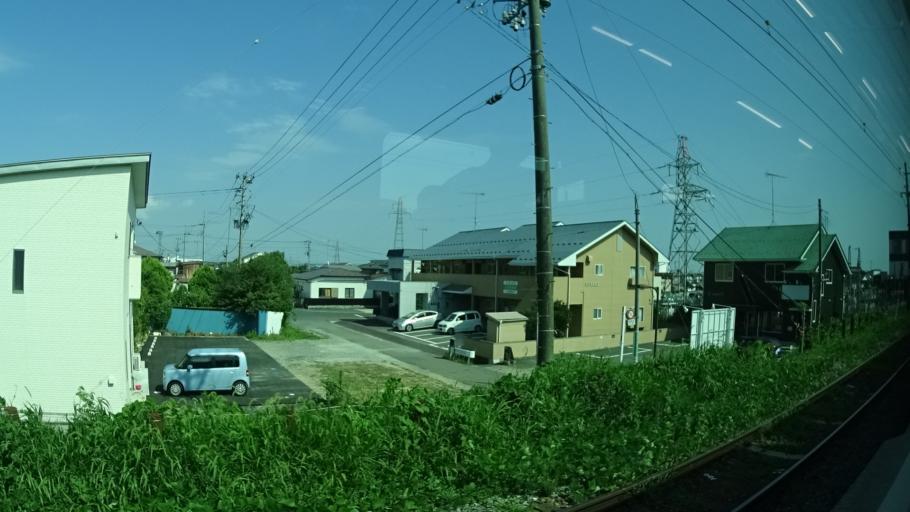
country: JP
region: Miyagi
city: Wakuya
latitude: 38.4759
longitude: 141.0984
